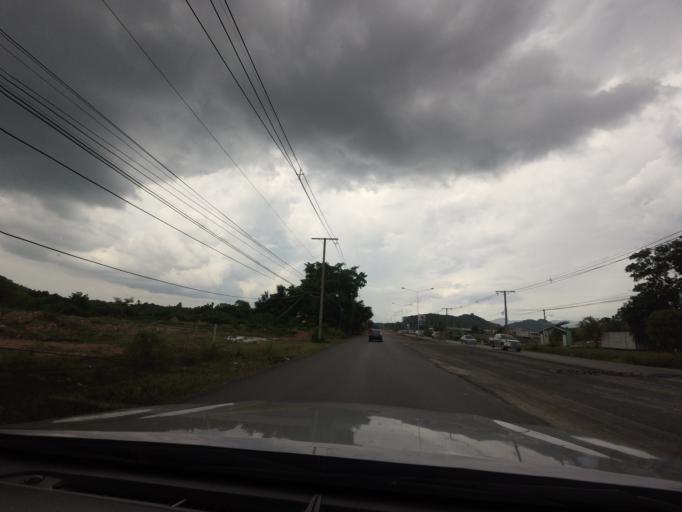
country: TH
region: Yala
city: Yala
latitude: 6.4827
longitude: 101.3163
